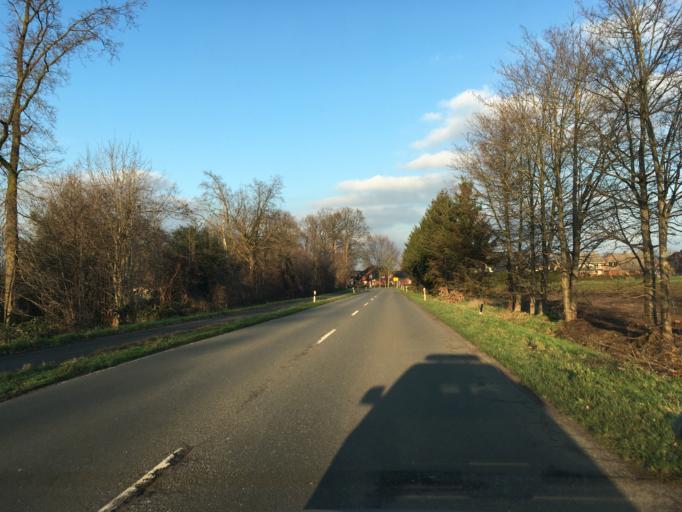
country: DE
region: North Rhine-Westphalia
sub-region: Regierungsbezirk Munster
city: Gronau
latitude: 52.1682
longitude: 7.0329
